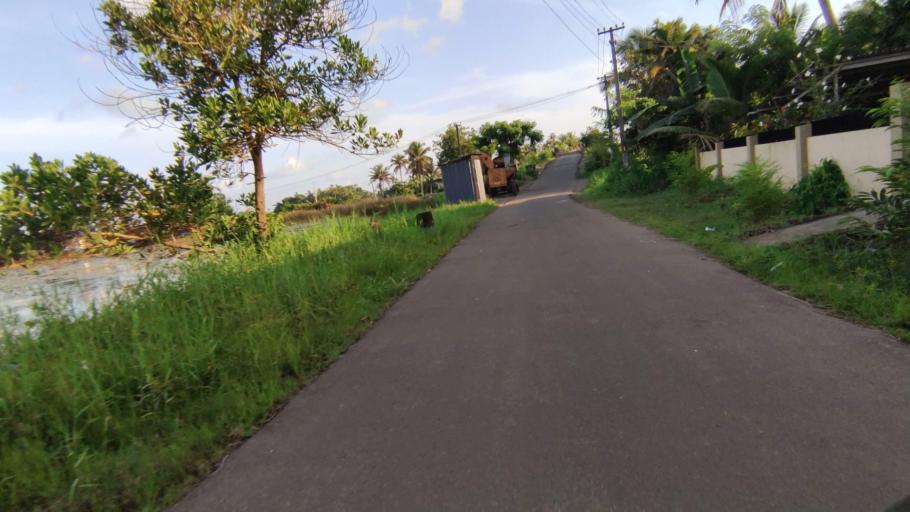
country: IN
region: Kerala
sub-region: Kottayam
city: Kottayam
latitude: 9.5897
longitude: 76.4483
